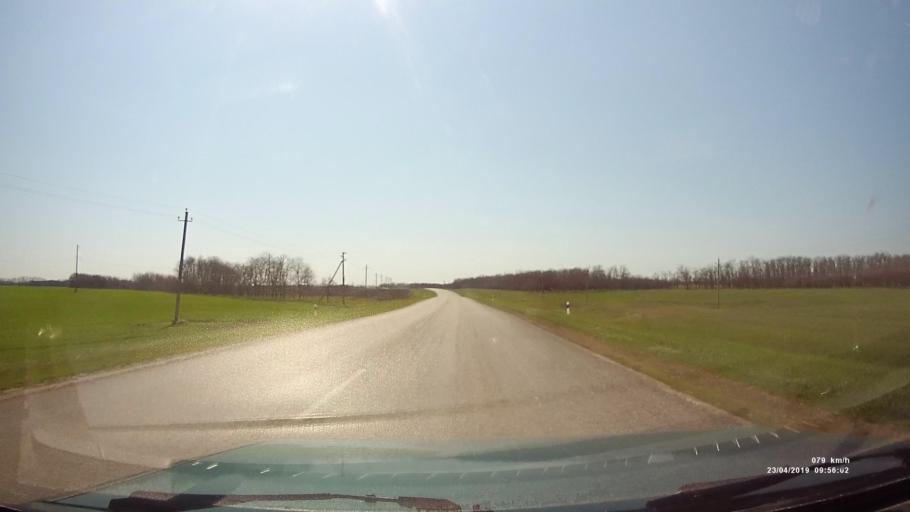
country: RU
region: Rostov
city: Orlovskiy
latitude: 46.8018
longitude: 42.0681
